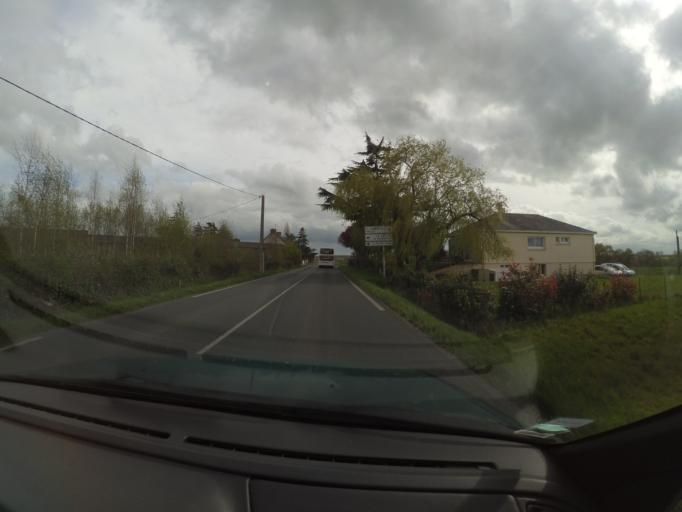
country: FR
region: Pays de la Loire
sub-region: Departement de Maine-et-Loire
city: Lire
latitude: 47.3149
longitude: -1.1629
